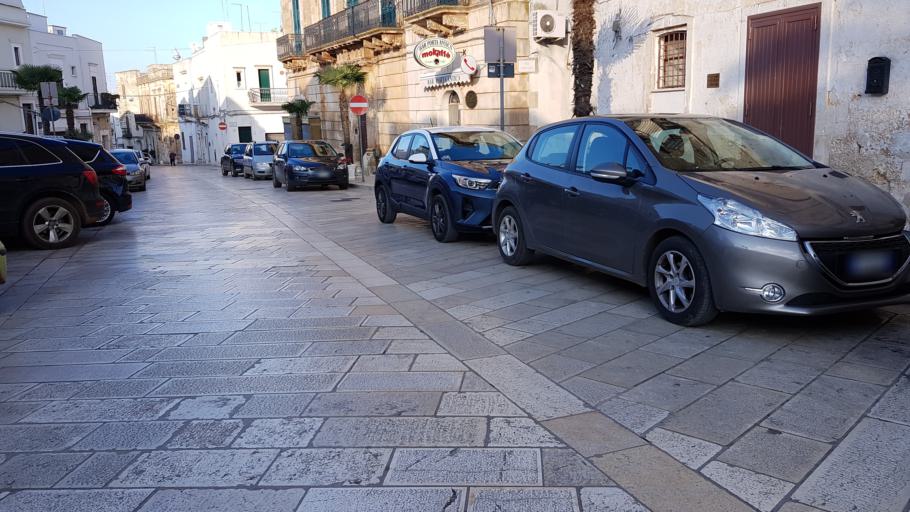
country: IT
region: Apulia
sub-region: Provincia di Brindisi
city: Carovigno
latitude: 40.7074
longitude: 17.6593
